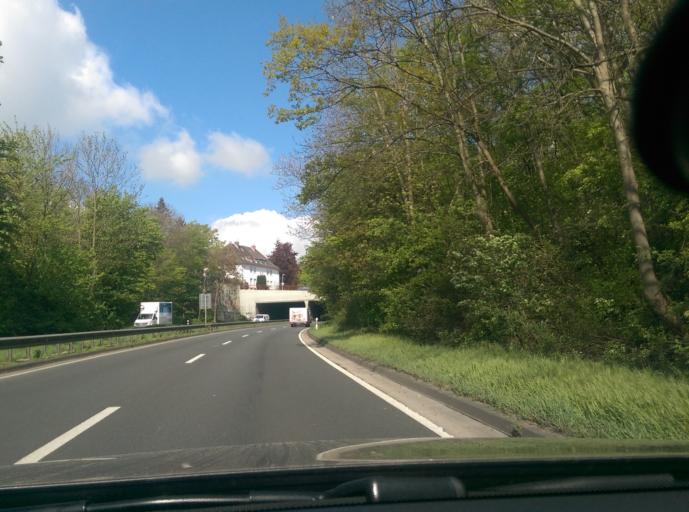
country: DE
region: Lower Saxony
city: Hannover
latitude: 52.3636
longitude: 9.7092
